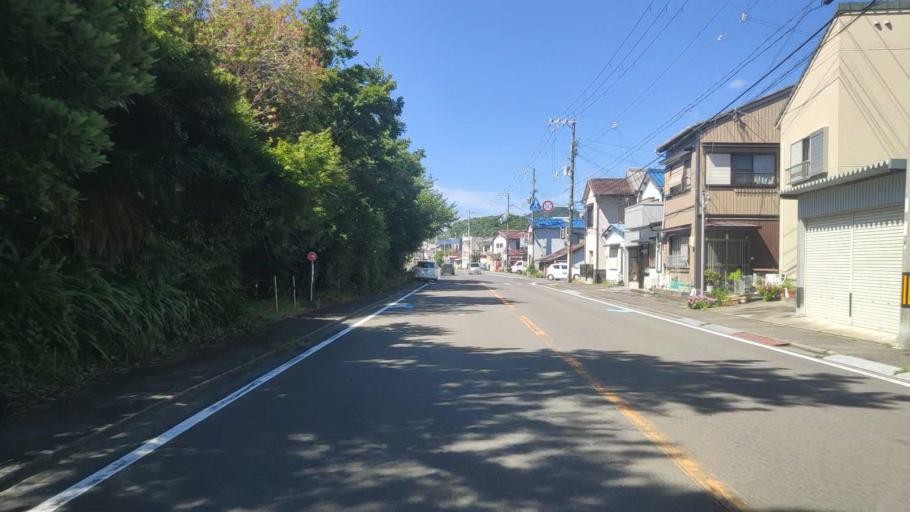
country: JP
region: Wakayama
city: Shingu
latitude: 33.7167
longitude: 136.0031
